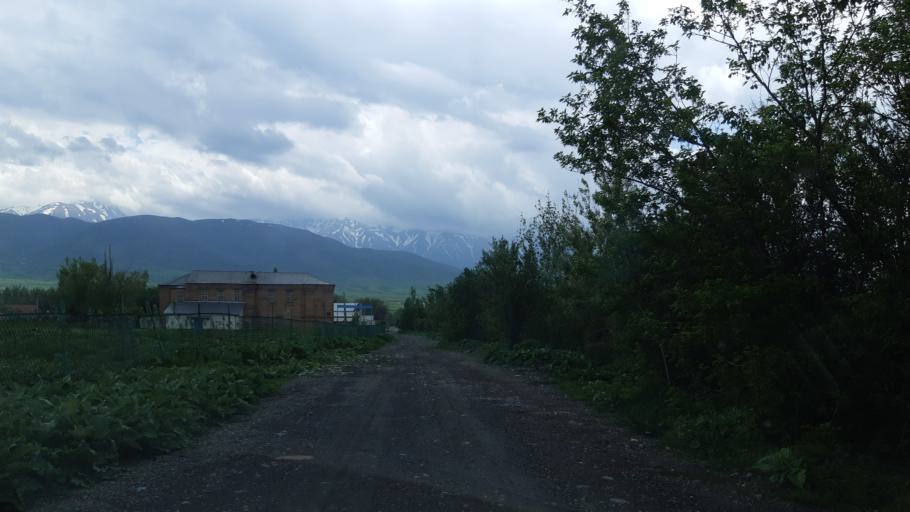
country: KZ
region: Ongtustik Qazaqstan
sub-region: Tulkibas Audany
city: Zhabagly
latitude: 42.5140
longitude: 70.5625
